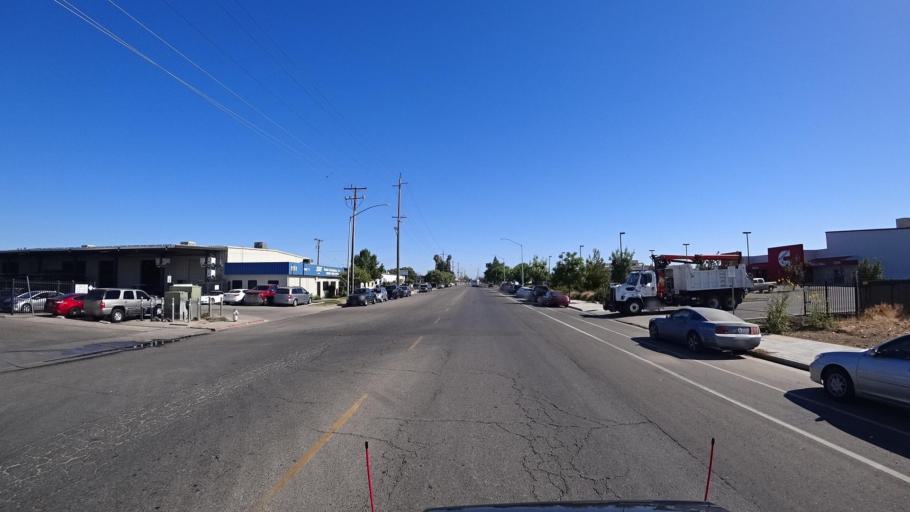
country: US
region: California
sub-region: Fresno County
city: Fresno
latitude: 36.7005
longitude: -119.7818
